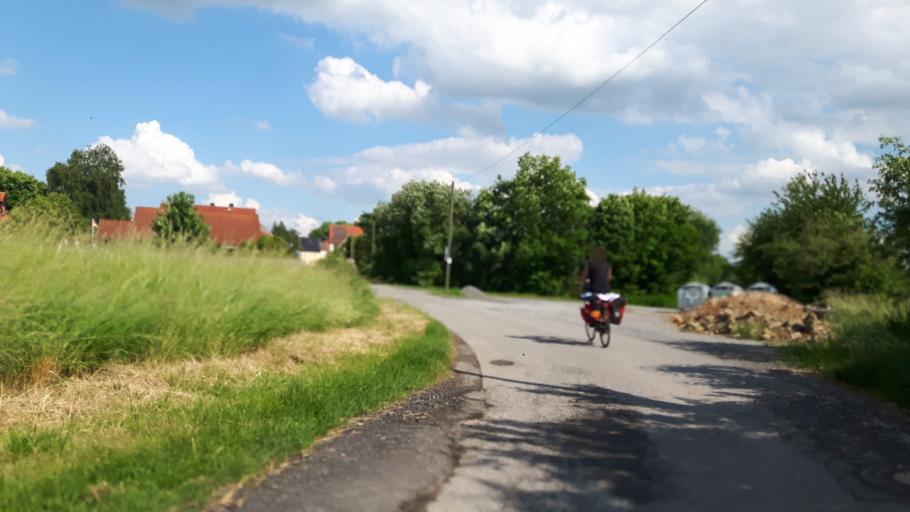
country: DE
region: Bavaria
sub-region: Regierungsbezirk Unterfranken
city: Geroldshausen
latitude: 49.6753
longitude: 9.8772
